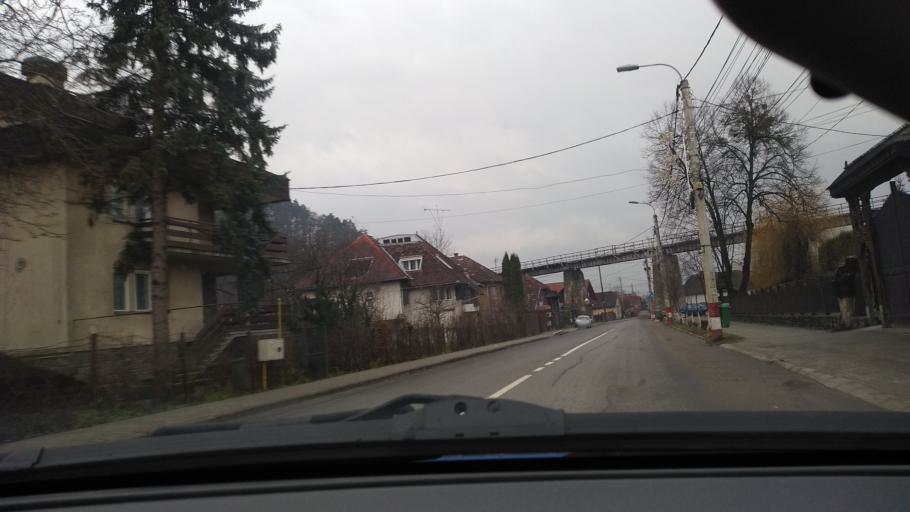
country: RO
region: Mures
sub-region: Oras Sovata
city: Sovata
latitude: 46.5912
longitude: 25.0718
